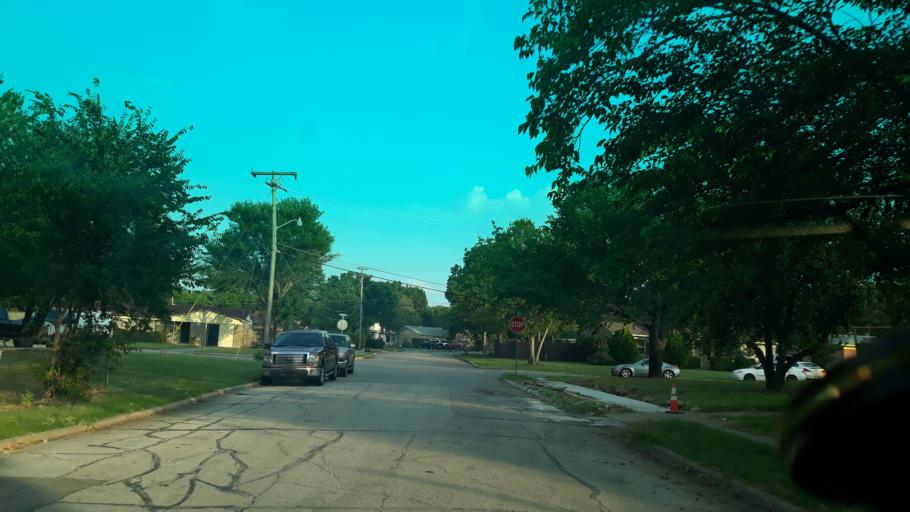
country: US
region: Texas
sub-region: Dallas County
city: Irving
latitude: 32.8465
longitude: -96.9783
